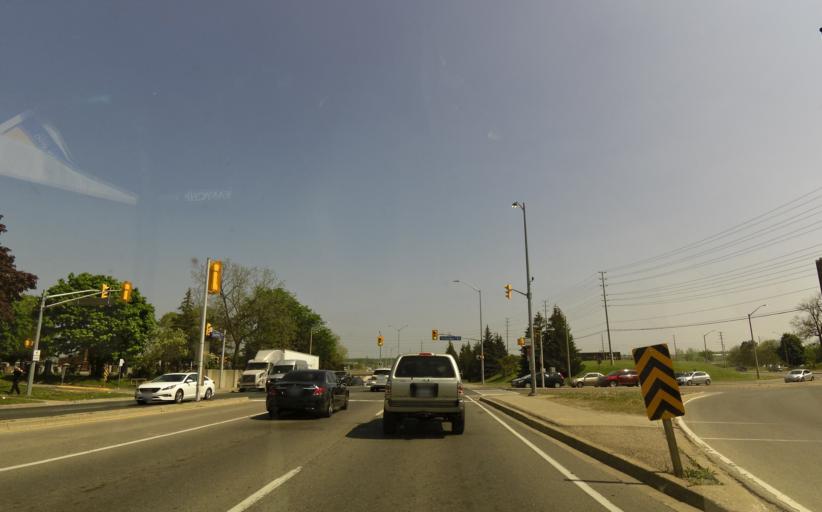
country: CA
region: Ontario
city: Mississauga
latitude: 43.5960
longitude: -79.6021
